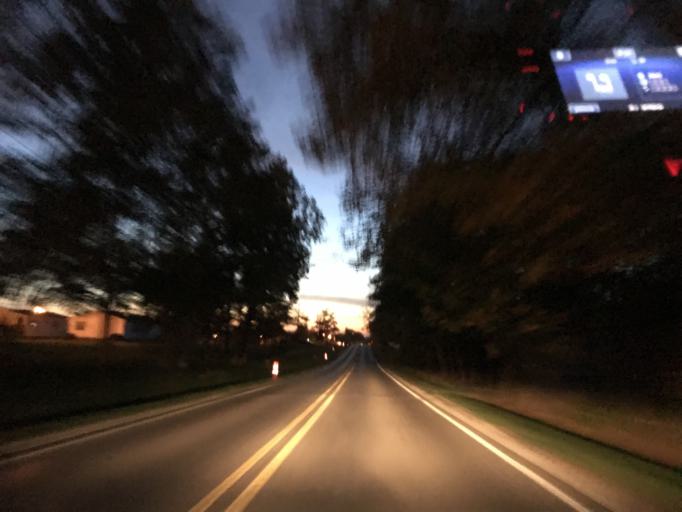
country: US
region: Michigan
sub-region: Oakland County
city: South Lyon
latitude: 42.4333
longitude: -83.6057
